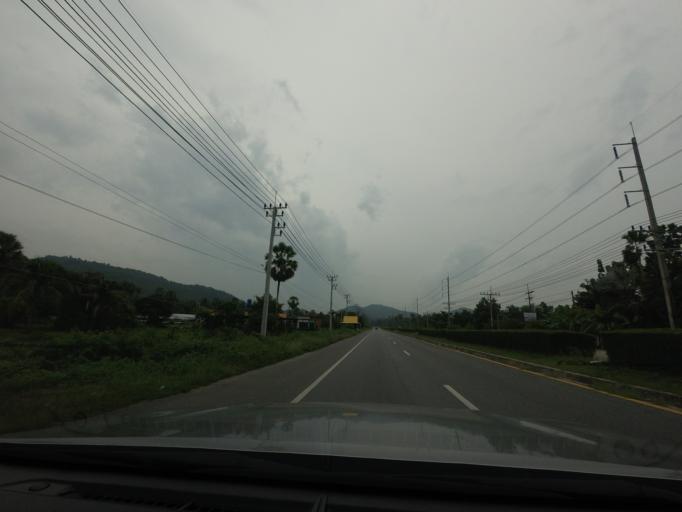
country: TH
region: Songkhla
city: Songkhla
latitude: 7.0855
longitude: 100.6282
